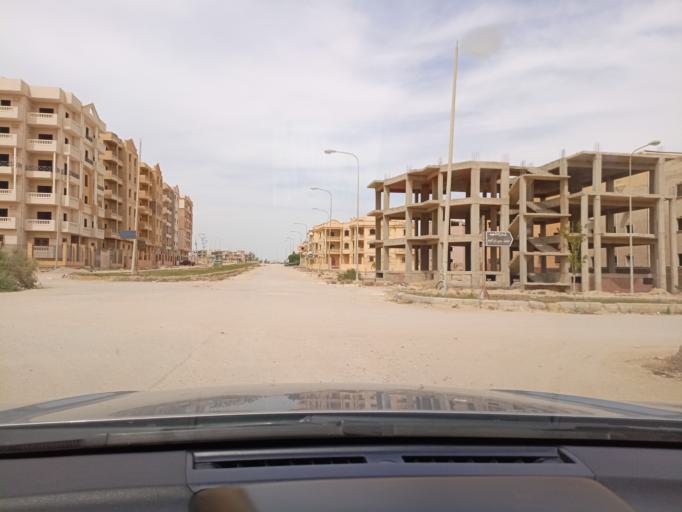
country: EG
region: Muhafazat al Qalyubiyah
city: Al Khankah
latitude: 30.2482
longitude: 31.5023
